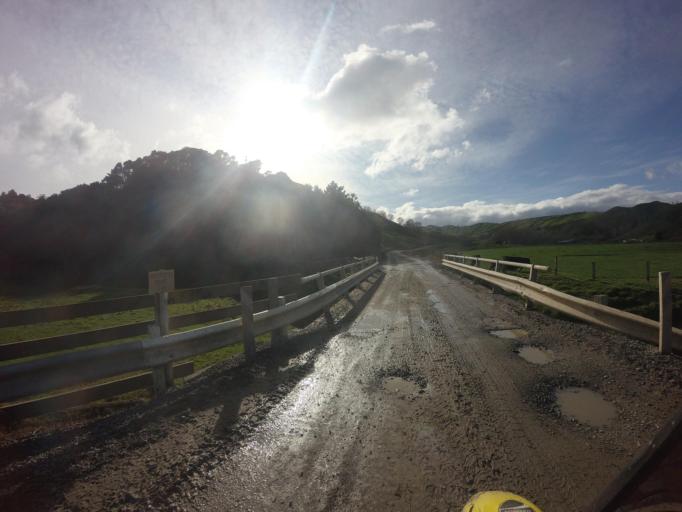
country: NZ
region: Hawke's Bay
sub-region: Wairoa District
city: Wairoa
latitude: -38.9933
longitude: 177.5896
